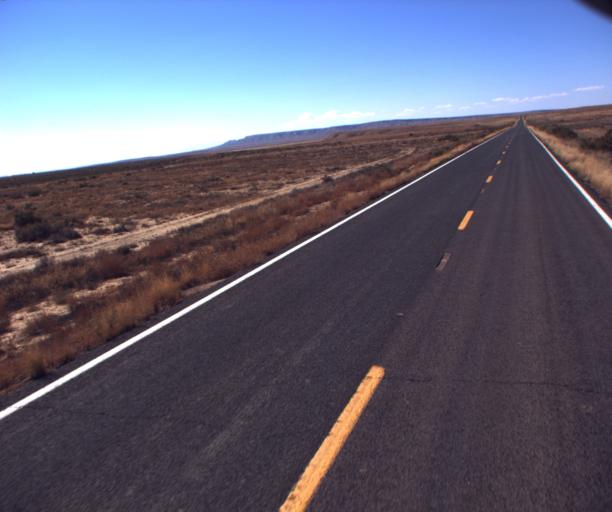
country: US
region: Arizona
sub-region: Navajo County
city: First Mesa
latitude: 35.9802
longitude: -110.7343
